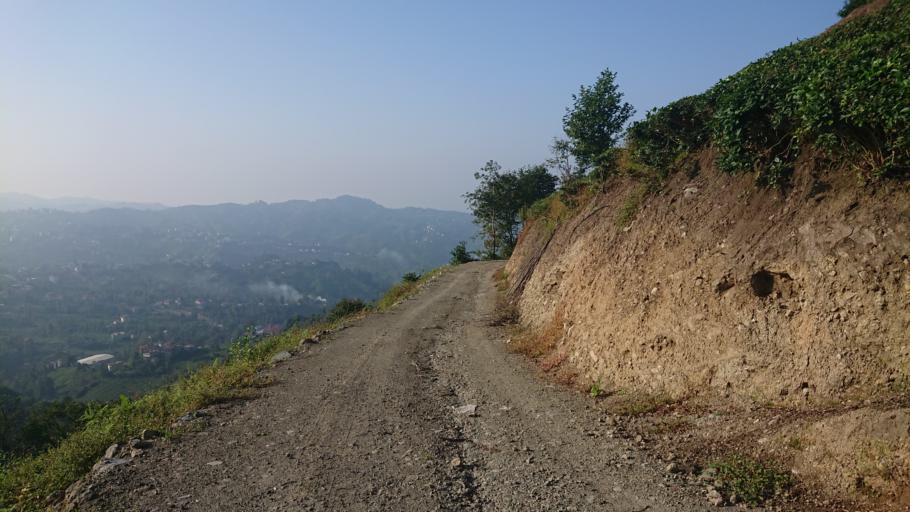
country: TR
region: Rize
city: Rize
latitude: 40.9855
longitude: 40.4986
